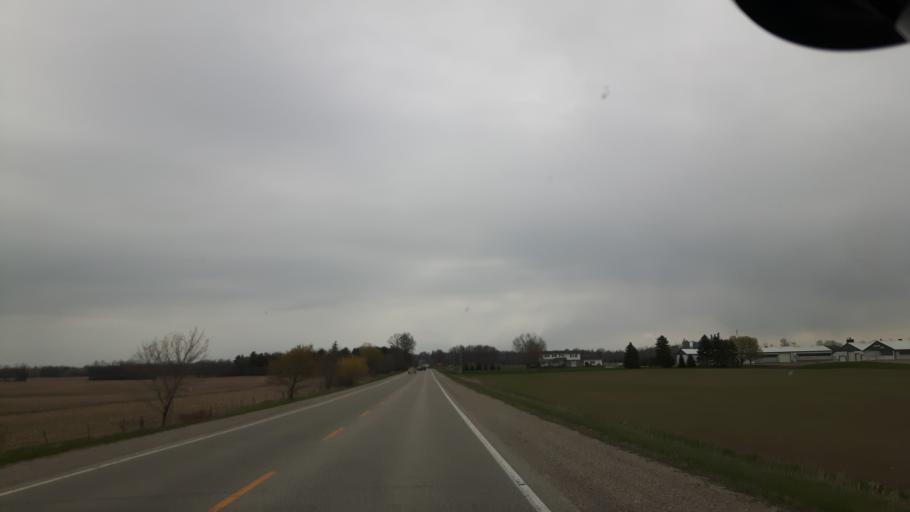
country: CA
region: Ontario
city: Bluewater
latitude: 43.6009
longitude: -81.5533
